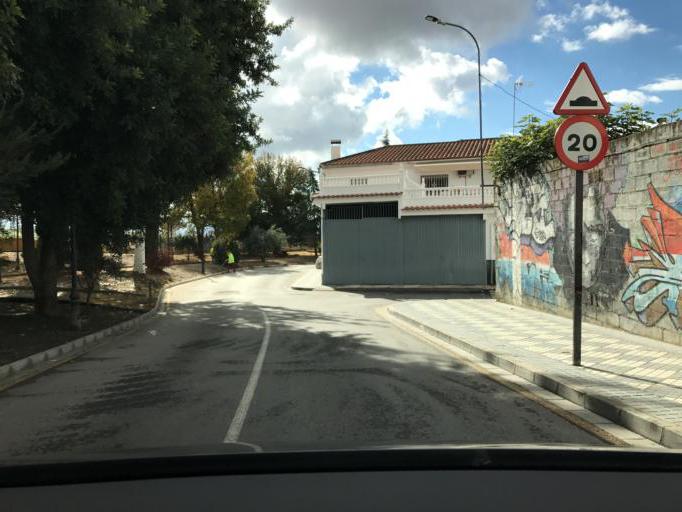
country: ES
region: Andalusia
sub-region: Provincia de Granada
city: Maracena
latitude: 37.2045
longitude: -3.6301
